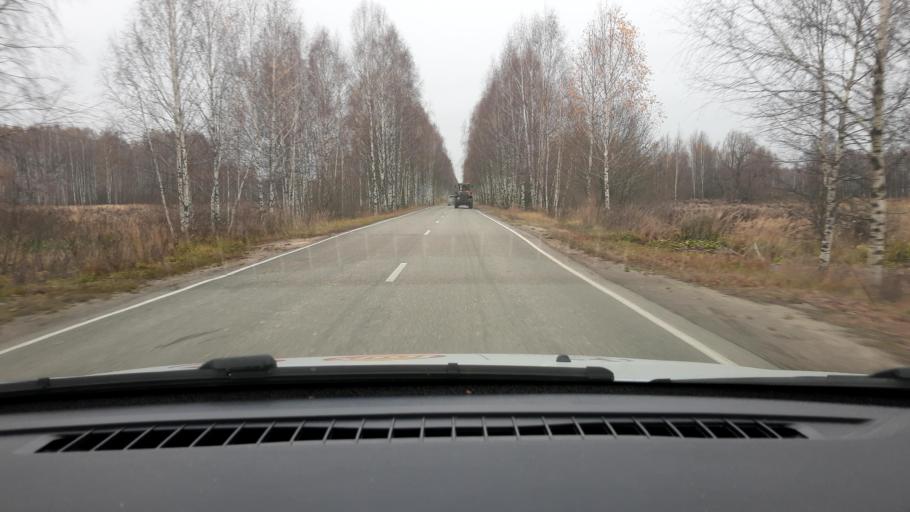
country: RU
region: Nizjnij Novgorod
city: Neklyudovo
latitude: 56.4822
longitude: 43.8693
